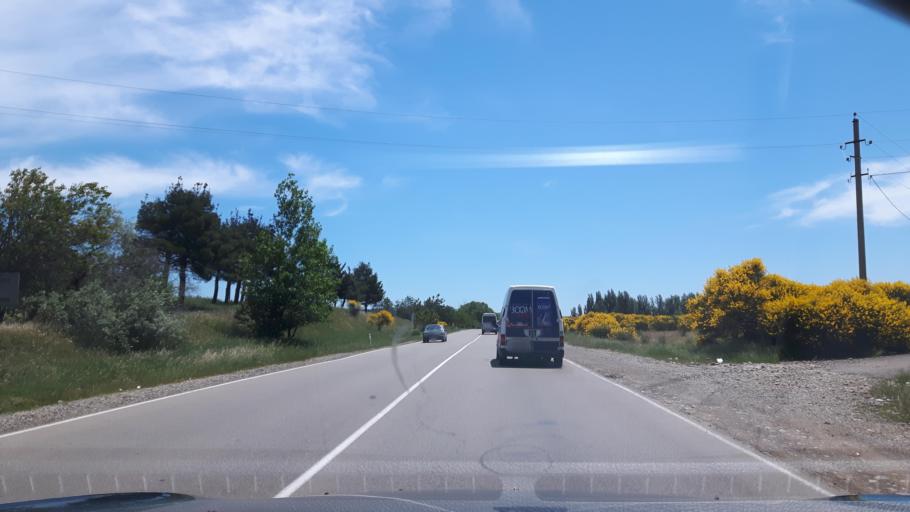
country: GE
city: Didi Lilo
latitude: 41.6962
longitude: 45.0533
